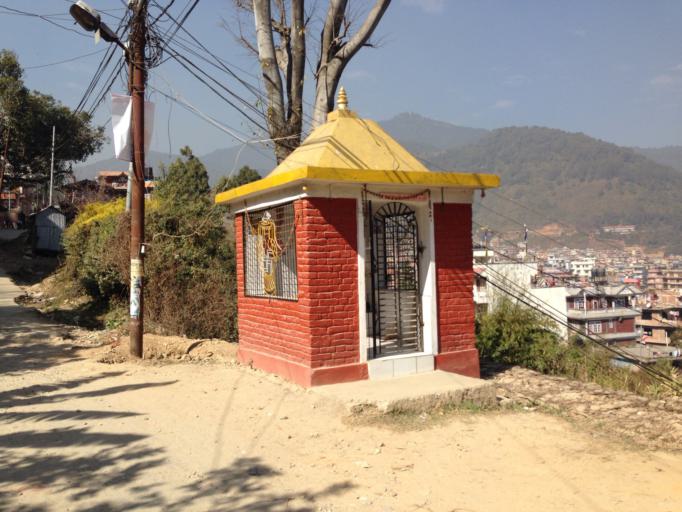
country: NP
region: Central Region
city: Kirtipur
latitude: 27.7185
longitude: 85.2807
